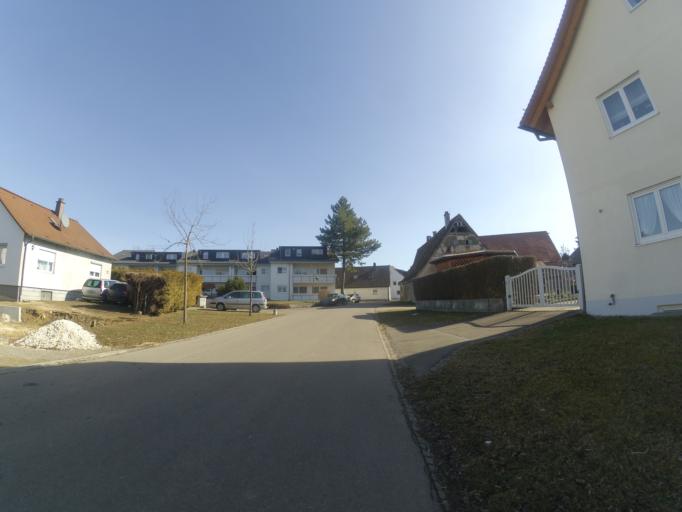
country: DE
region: Baden-Wuerttemberg
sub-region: Tuebingen Region
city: Langenau
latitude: 48.5023
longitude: 10.1394
